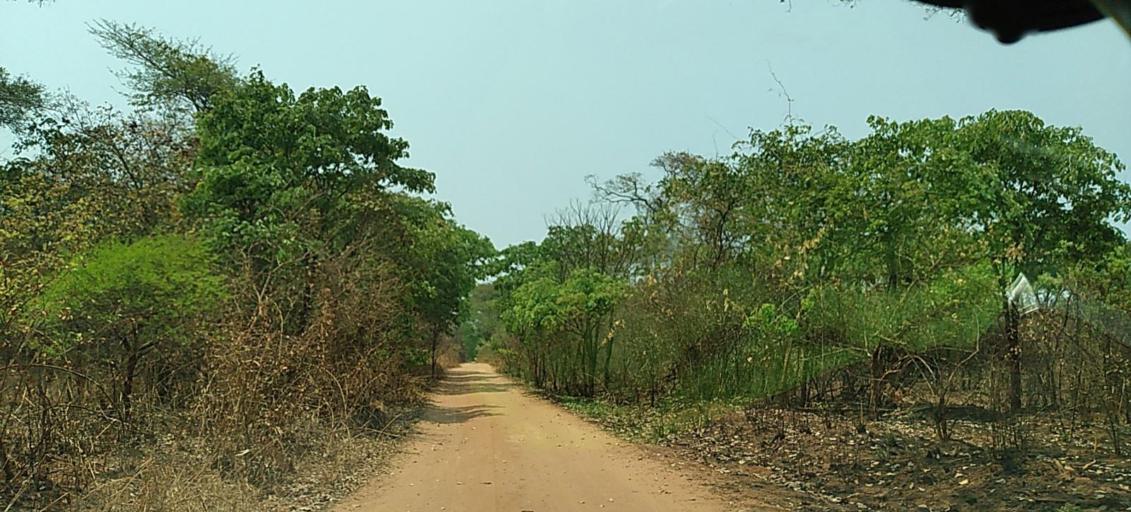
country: ZM
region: North-Western
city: Kabompo
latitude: -13.7060
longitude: 24.3227
